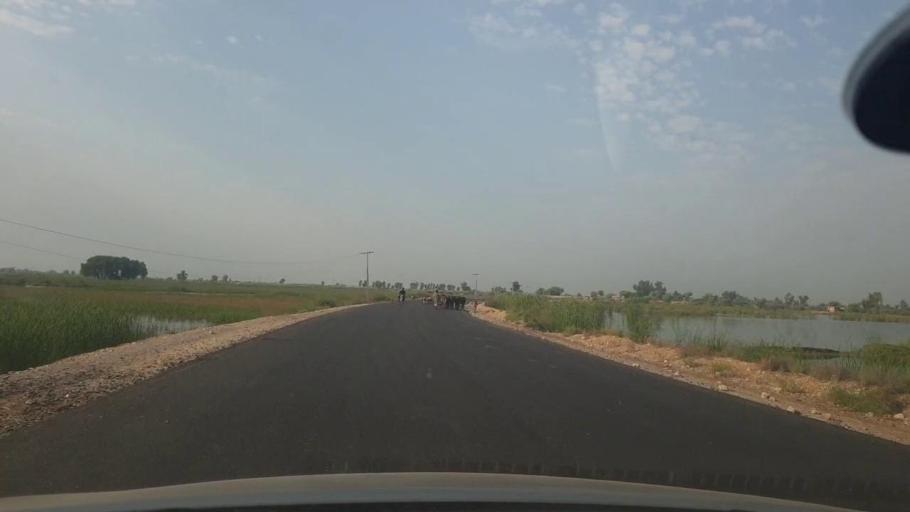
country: PK
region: Sindh
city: Jacobabad
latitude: 28.0955
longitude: 68.3300
